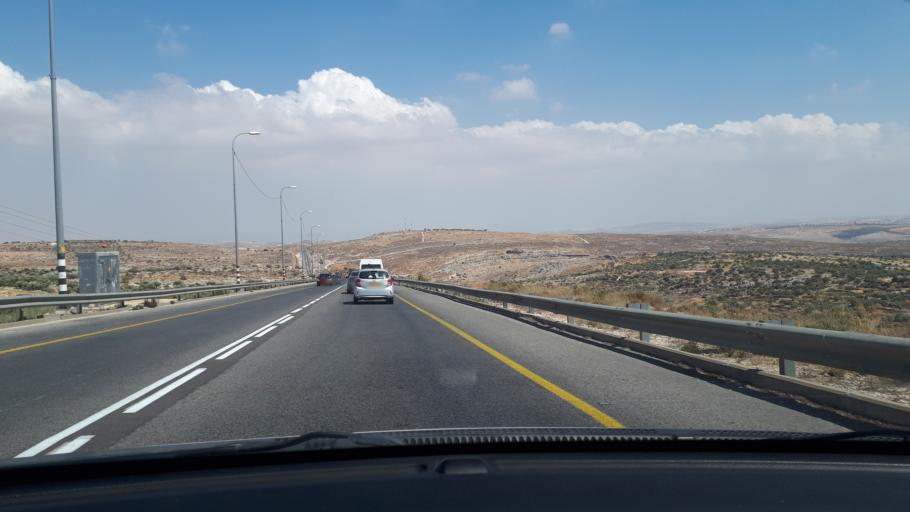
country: PS
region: West Bank
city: Burqah
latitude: 31.9036
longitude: 35.2579
